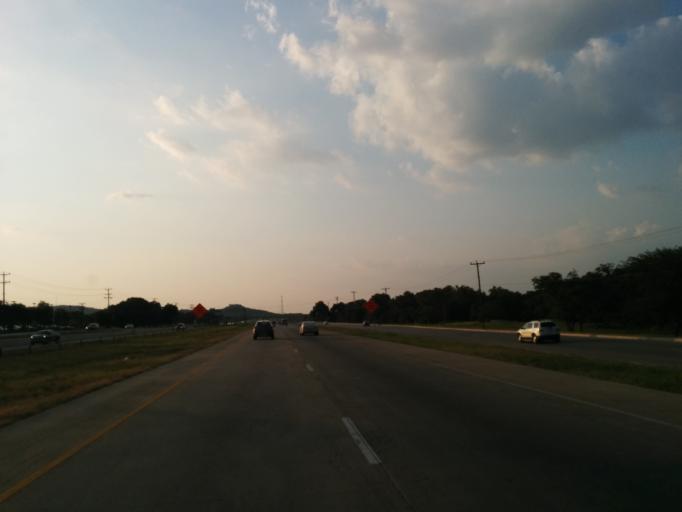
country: US
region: Texas
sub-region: Bexar County
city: Cross Mountain
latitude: 29.6413
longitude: -98.6177
